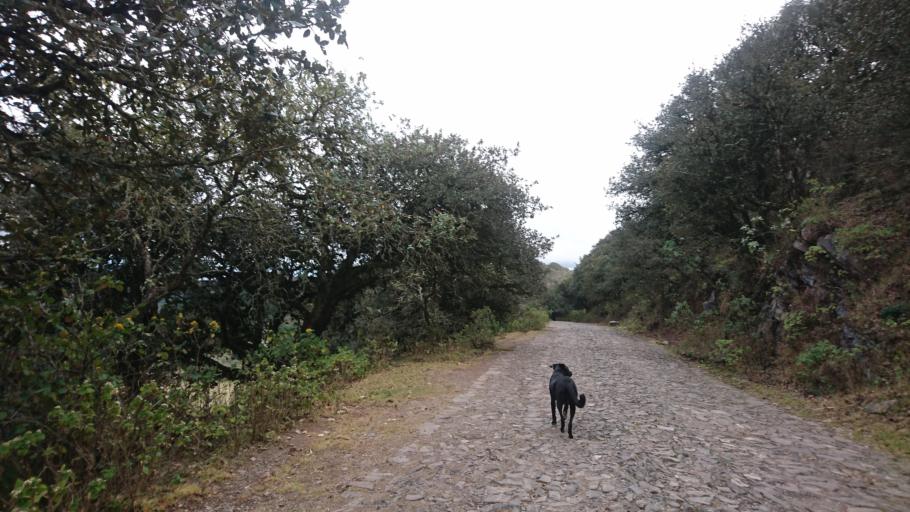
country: MX
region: San Luis Potosi
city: Zaragoza
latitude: 22.0744
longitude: -100.6395
